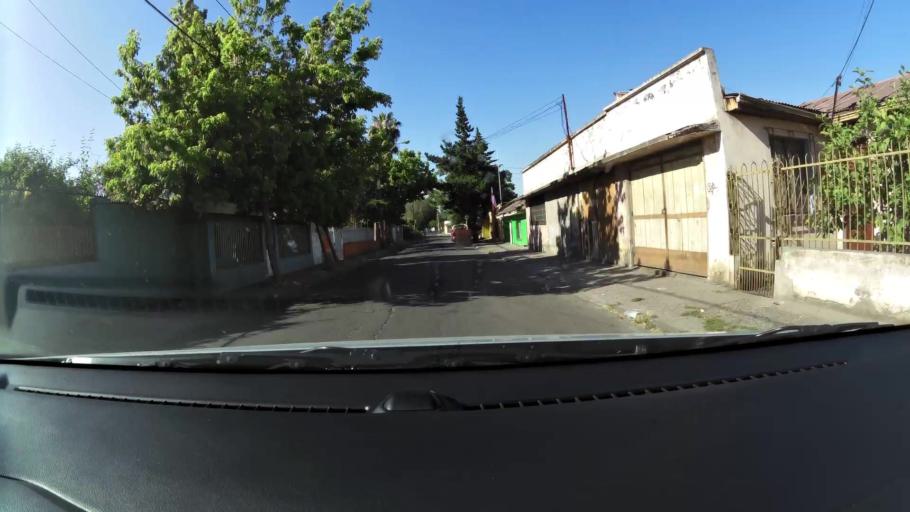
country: CL
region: Santiago Metropolitan
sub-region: Provincia de Maipo
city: San Bernardo
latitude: -33.5480
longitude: -70.6838
